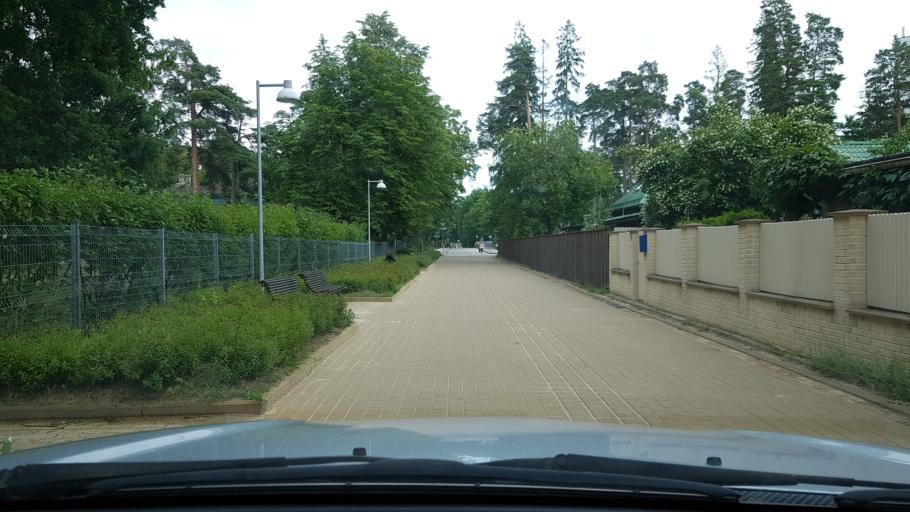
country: EE
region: Ida-Virumaa
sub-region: Narva-Joesuu linn
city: Narva-Joesuu
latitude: 59.4536
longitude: 28.0257
